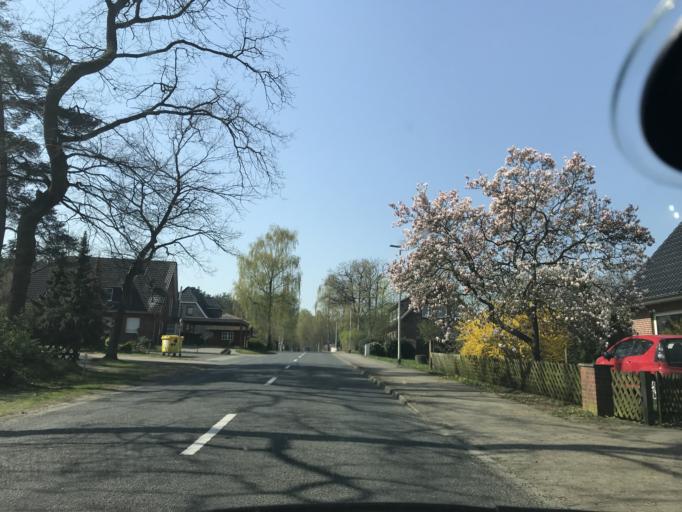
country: DE
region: Lower Saxony
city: Buxtehude
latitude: 53.4517
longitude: 9.7374
